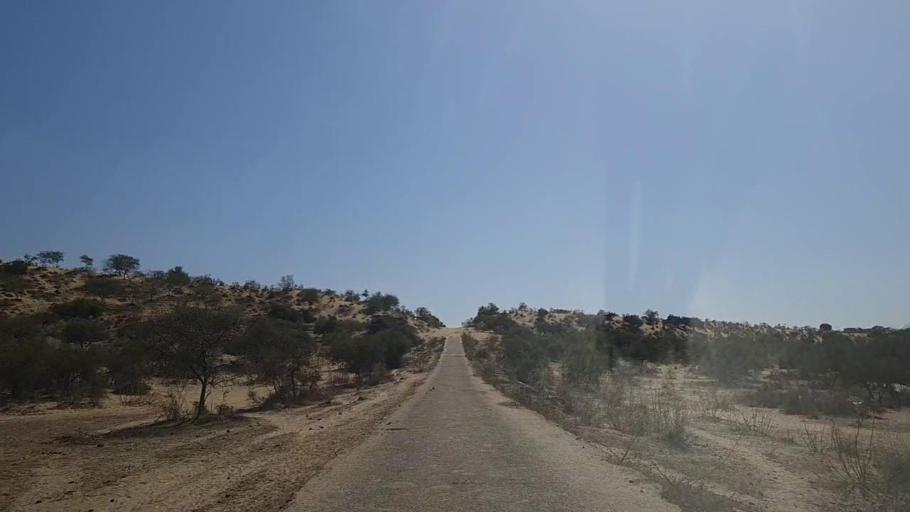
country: PK
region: Sindh
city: Naukot
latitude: 24.8320
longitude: 69.6061
